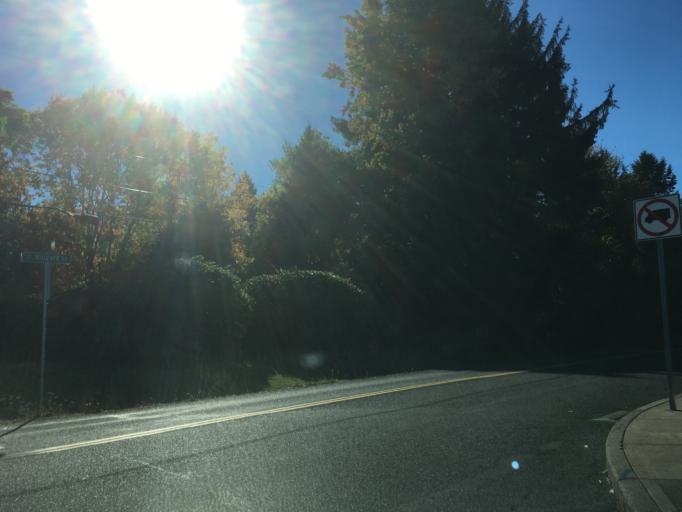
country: US
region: Oregon
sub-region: Multnomah County
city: Gresham
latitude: 45.4771
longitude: -122.3932
